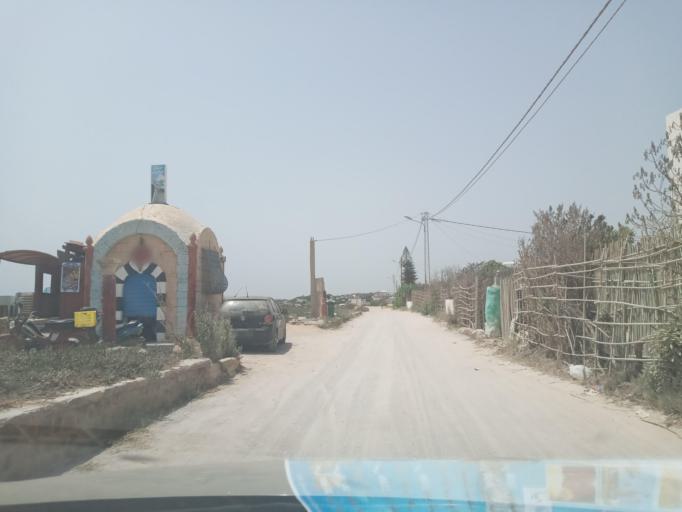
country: TN
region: Nabul
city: El Haouaria
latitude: 37.0349
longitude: 11.0586
